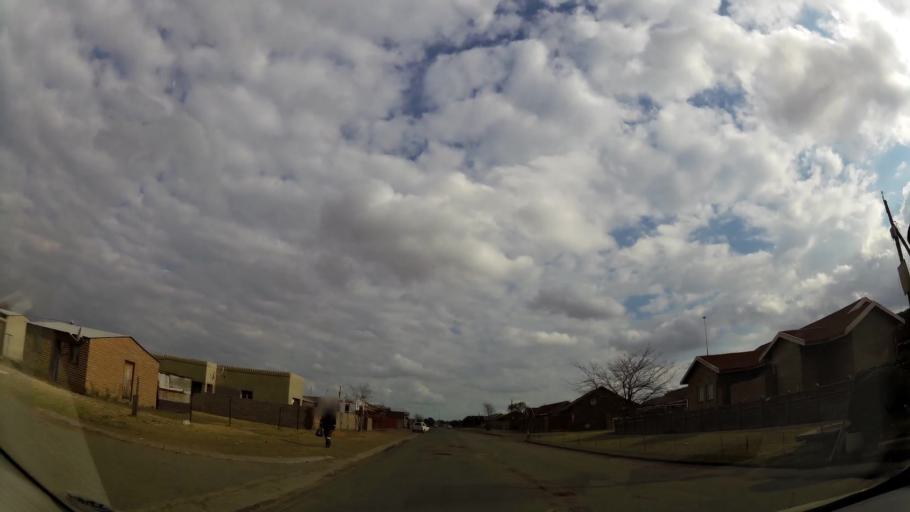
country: ZA
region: Orange Free State
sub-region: Fezile Dabi District Municipality
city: Sasolburg
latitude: -26.8382
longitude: 27.8590
